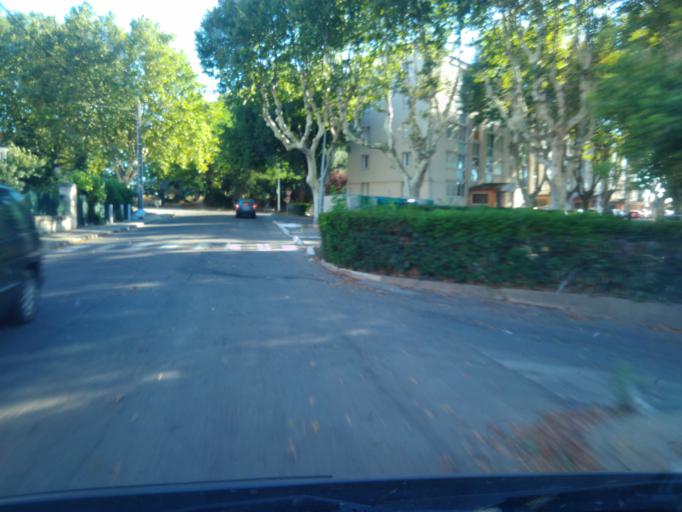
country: FR
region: Languedoc-Roussillon
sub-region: Departement du Gard
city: Saint-Gilles
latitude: 43.6720
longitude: 4.4321
